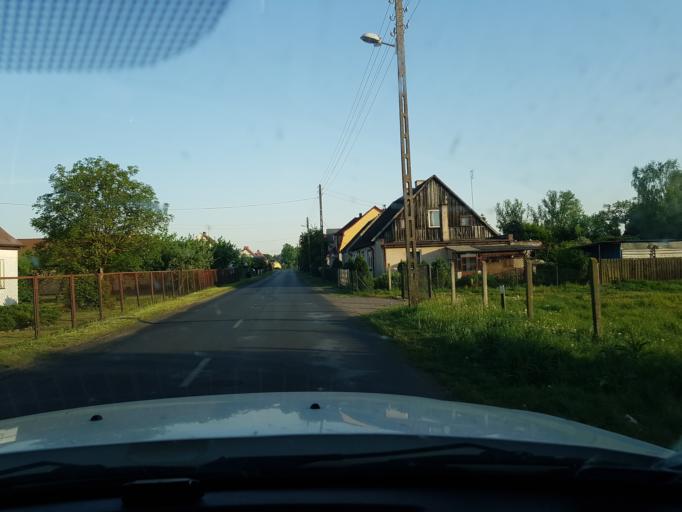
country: PL
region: West Pomeranian Voivodeship
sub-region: Powiat stargardzki
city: Kobylanka
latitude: 53.4238
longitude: 14.9026
